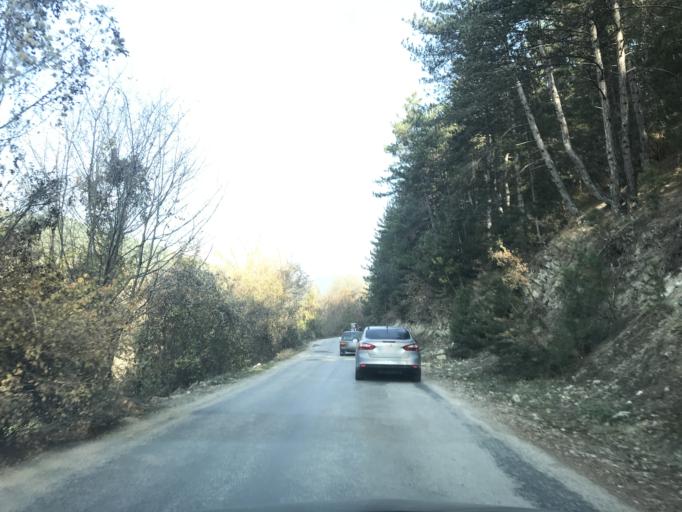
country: TR
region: Bolu
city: Bolu
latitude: 40.7890
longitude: 31.6371
